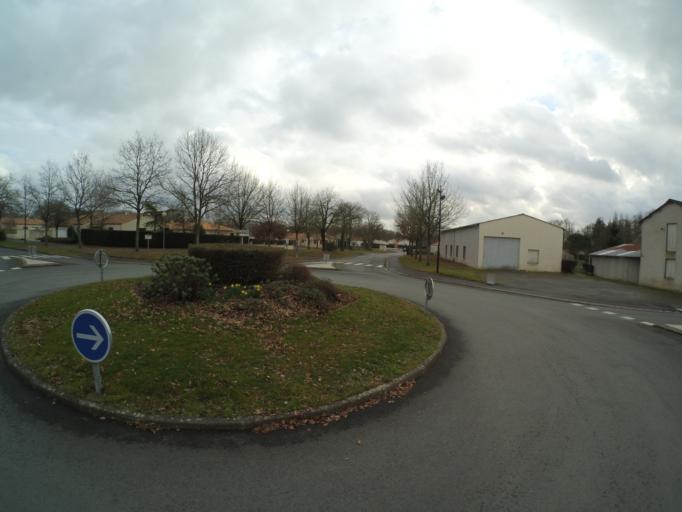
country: FR
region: Pays de la Loire
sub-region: Departement de la Vendee
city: Saint-Hilaire-de-Loulay
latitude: 47.0037
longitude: -1.3269
